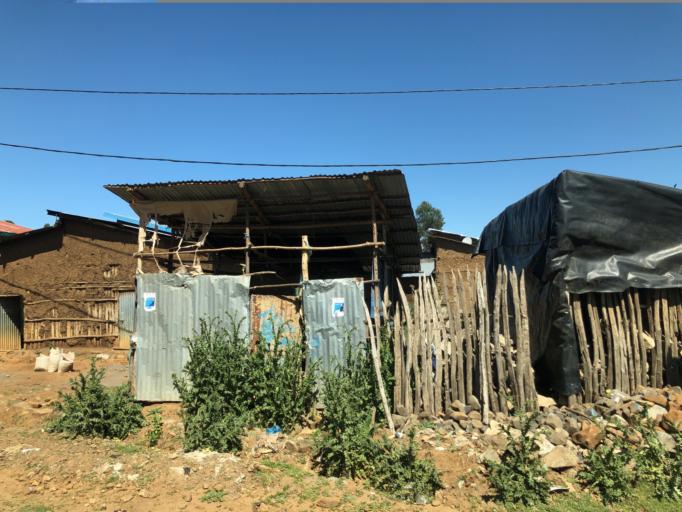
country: ET
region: Amhara
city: Lalibela
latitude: 11.6897
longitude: 38.9228
